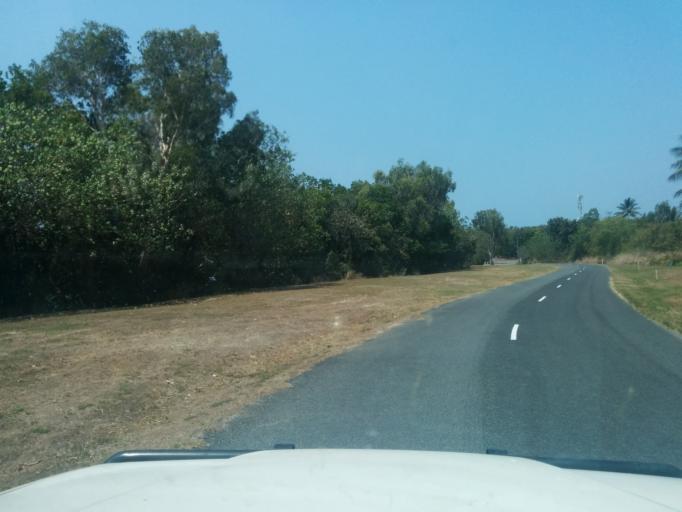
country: AU
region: Queensland
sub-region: Cairns
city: Redlynch
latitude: -16.8723
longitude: 145.7354
